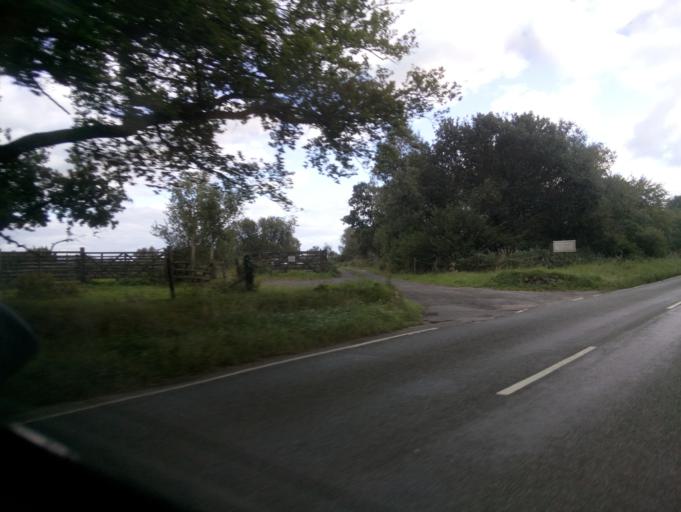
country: GB
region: England
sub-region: Devon
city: Honiton
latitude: 50.7715
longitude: -3.2108
